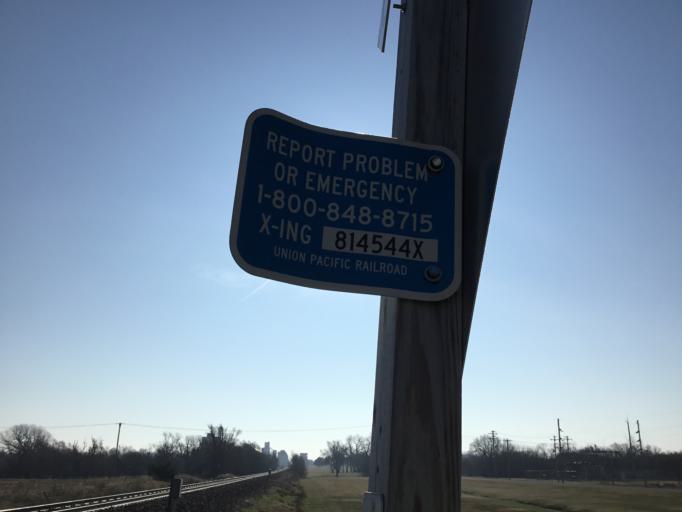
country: US
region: Kansas
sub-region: Ellsworth County
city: Ellsworth
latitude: 38.8268
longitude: -98.4851
